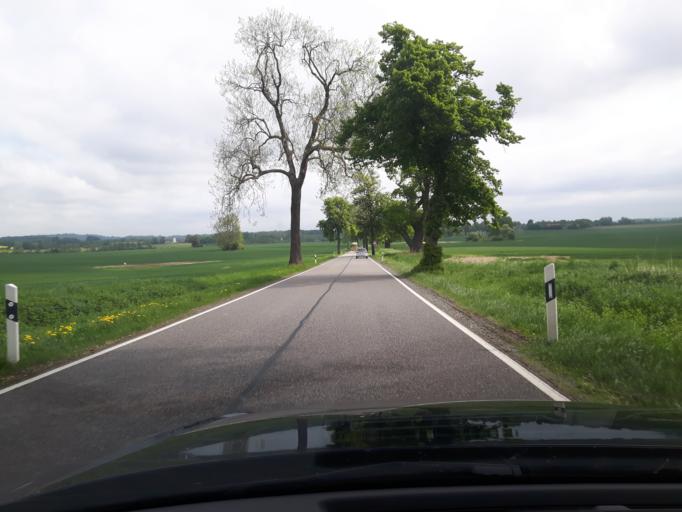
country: DE
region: Mecklenburg-Vorpommern
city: Gross Wokern
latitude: 53.6588
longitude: 12.5076
